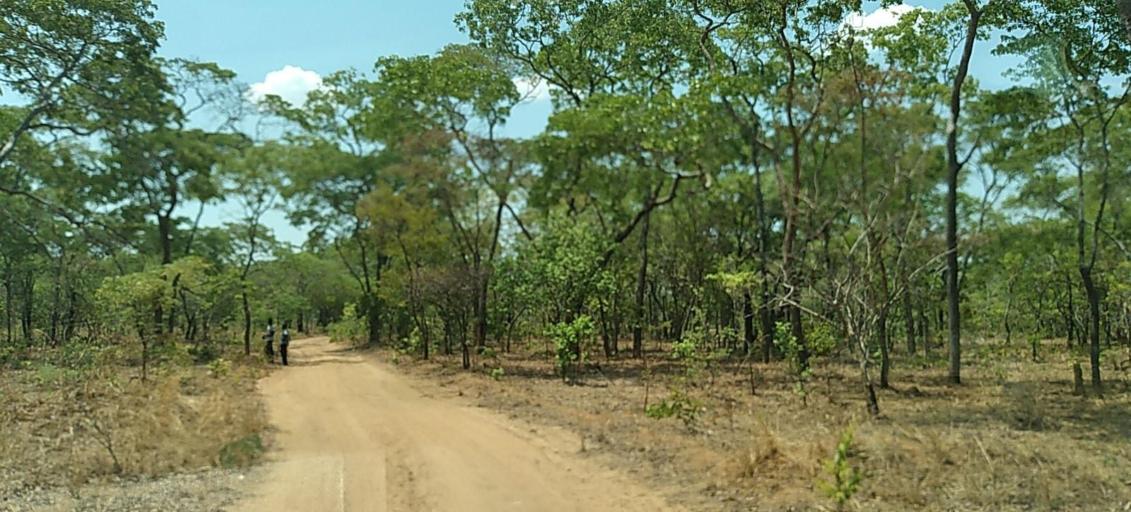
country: ZM
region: Copperbelt
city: Mpongwe
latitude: -13.6481
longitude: 28.4861
